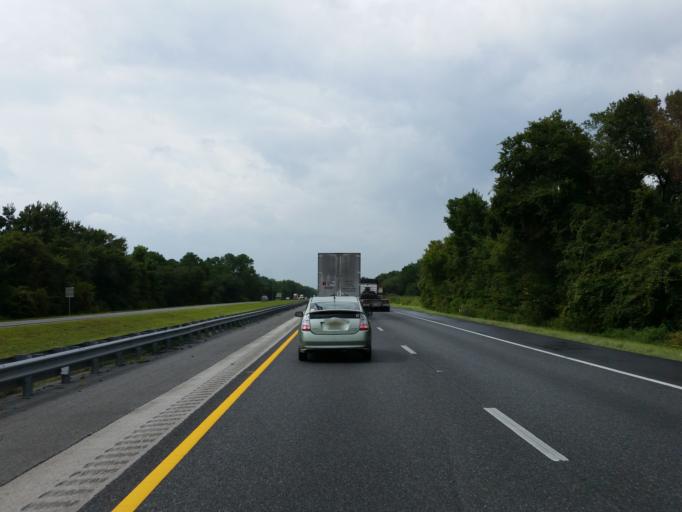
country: US
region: Florida
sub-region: Sumter County
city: Wildwood
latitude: 28.8414
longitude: -82.0904
